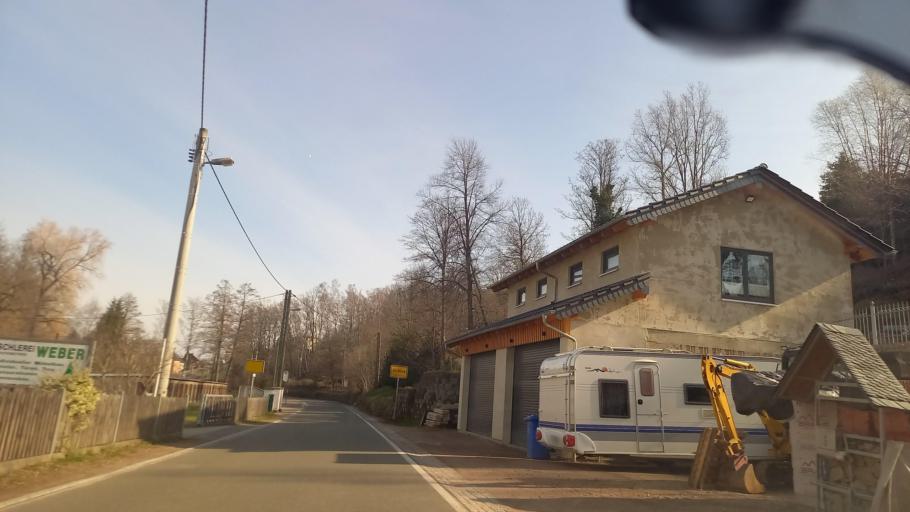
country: DE
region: Saxony
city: Kirchberg
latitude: 50.6139
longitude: 12.5210
